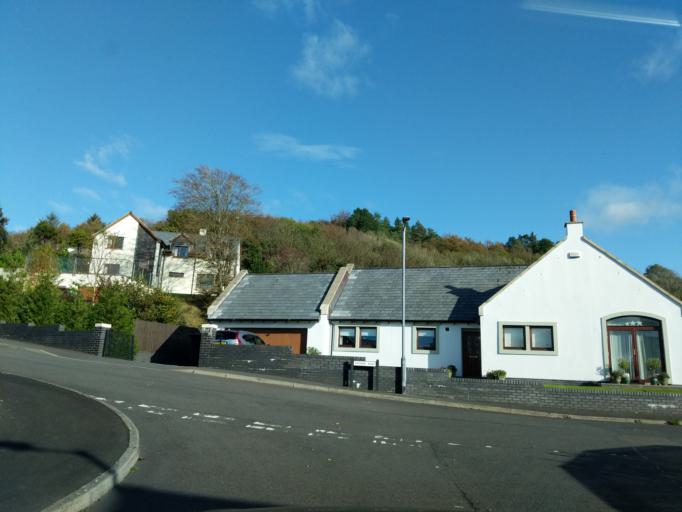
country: GB
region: Scotland
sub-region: Dumfries and Galloway
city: Kirkcudbright
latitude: 54.8306
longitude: -4.0500
